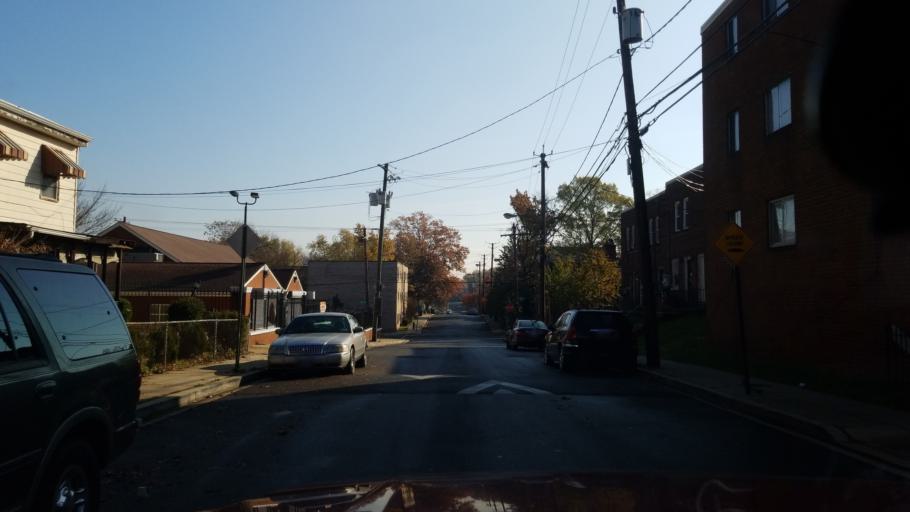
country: US
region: Maryland
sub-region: Prince George's County
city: Capitol Heights
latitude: 38.8858
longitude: -76.9292
